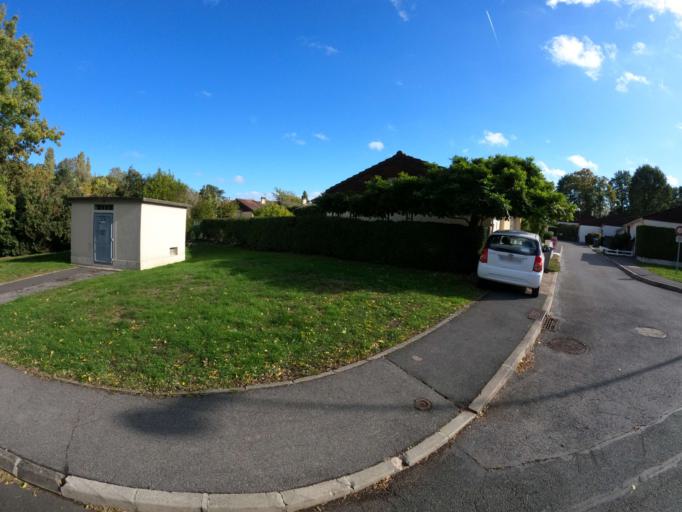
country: FR
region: Ile-de-France
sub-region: Departement de Seine-et-Marne
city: Coupvray
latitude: 48.8906
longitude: 2.8109
